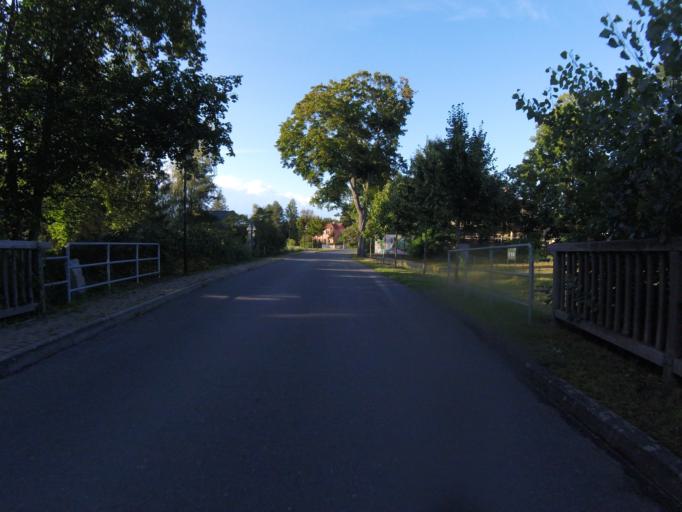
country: DE
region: Brandenburg
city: Munchehofe
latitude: 52.2178
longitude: 13.7750
